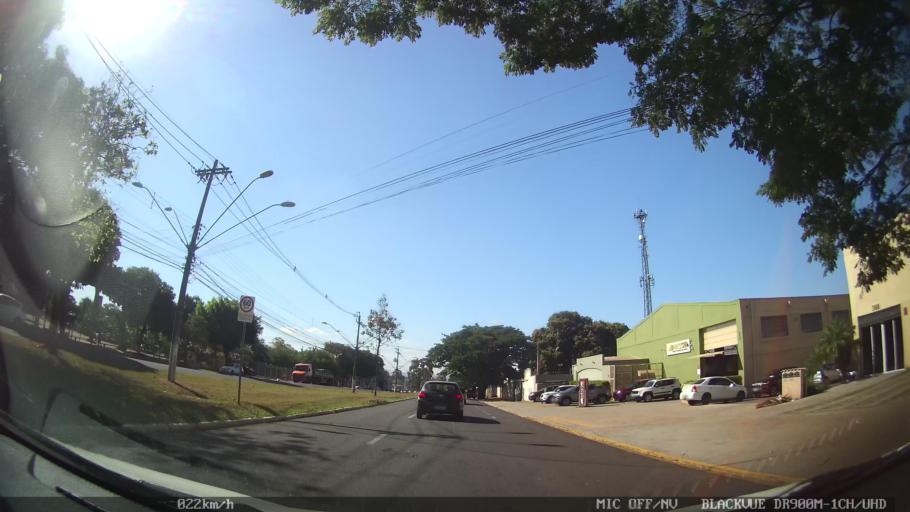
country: BR
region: Sao Paulo
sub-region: Ribeirao Preto
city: Ribeirao Preto
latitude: -21.1994
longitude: -47.7659
